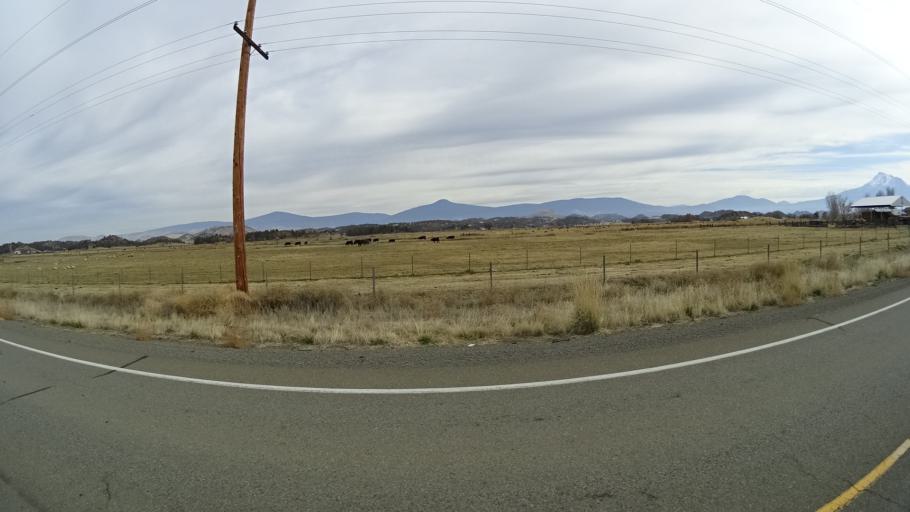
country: US
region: California
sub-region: Siskiyou County
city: Montague
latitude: 41.6631
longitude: -122.5214
